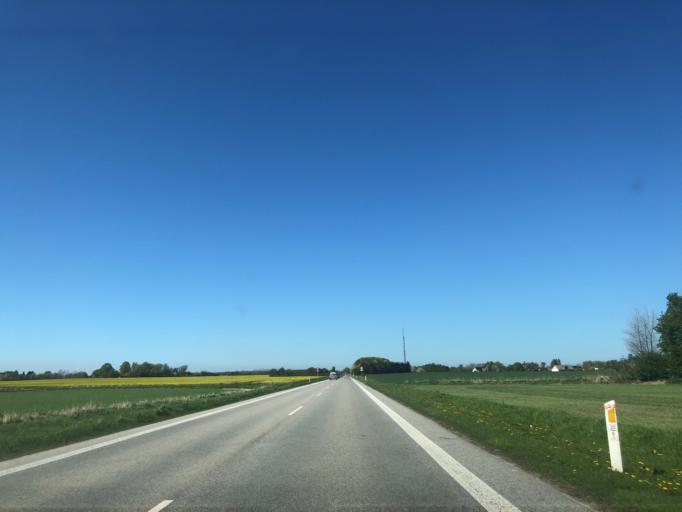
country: DK
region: Zealand
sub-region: Stevns Kommune
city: Store Heddinge
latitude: 55.3163
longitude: 12.3678
